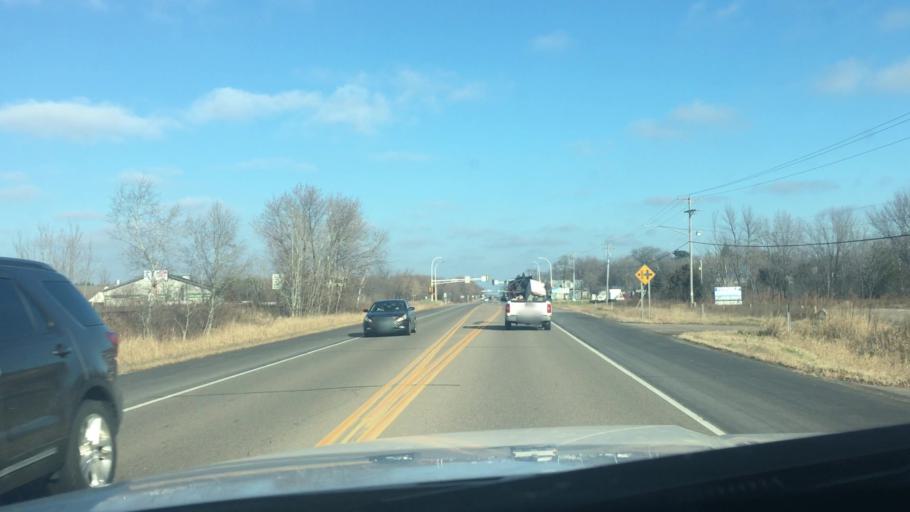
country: US
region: Minnesota
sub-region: Washington County
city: Hugo
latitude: 45.1505
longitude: -92.9960
